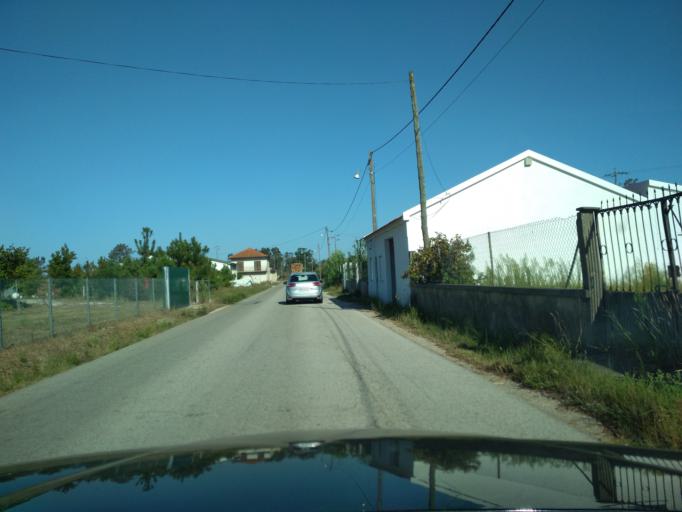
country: PT
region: Coimbra
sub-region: Figueira da Foz
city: Lavos
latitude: 40.0526
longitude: -8.8669
